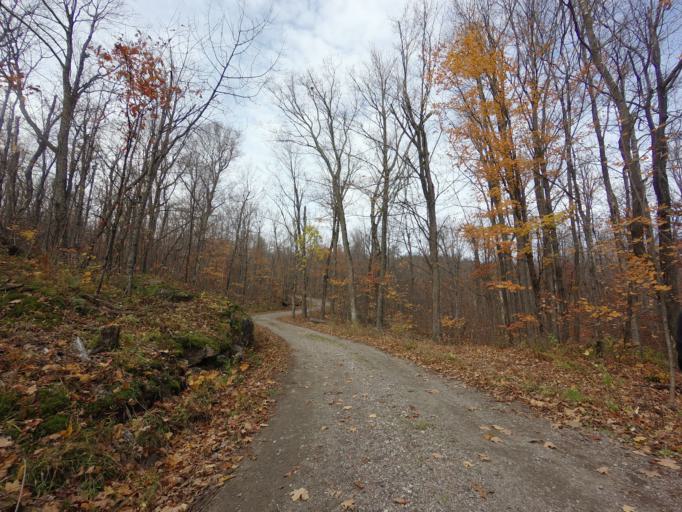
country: CA
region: Quebec
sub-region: Outaouais
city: Wakefield
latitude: 45.5330
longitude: -75.9414
